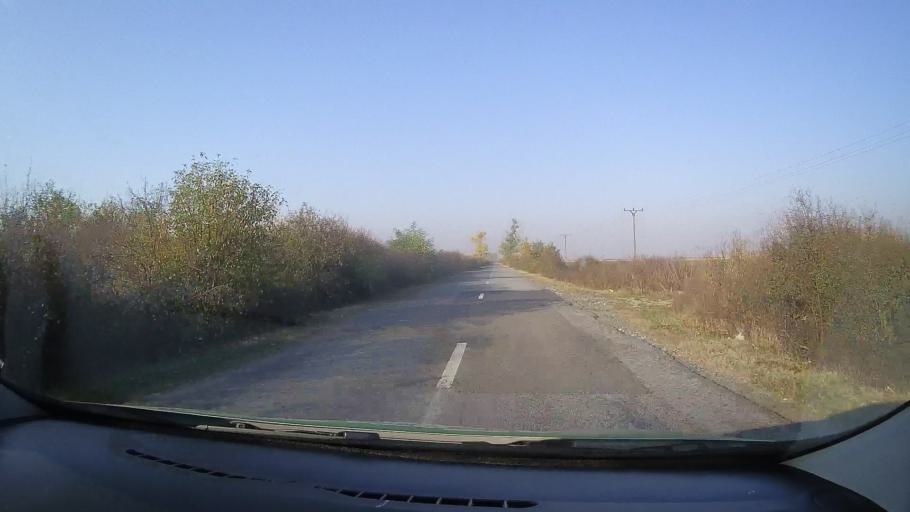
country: RO
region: Arad
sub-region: Comuna Socodor
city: Socodor
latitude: 46.5035
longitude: 21.4089
